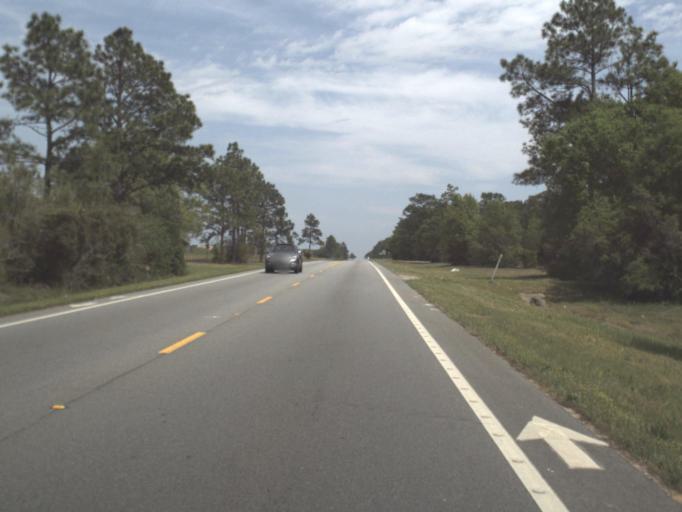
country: US
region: Florida
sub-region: Escambia County
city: Cantonment
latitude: 30.5353
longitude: -87.3689
